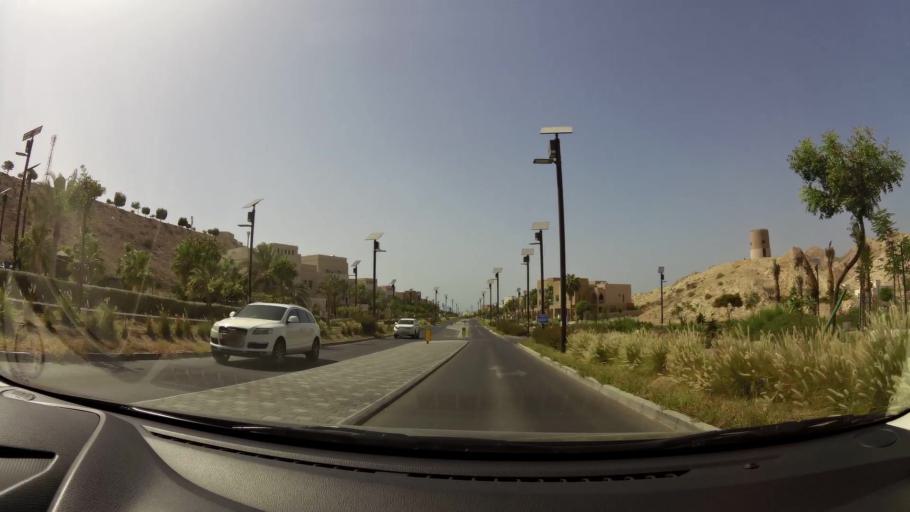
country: OM
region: Muhafazat Masqat
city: Muscat
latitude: 23.6266
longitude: 58.5038
